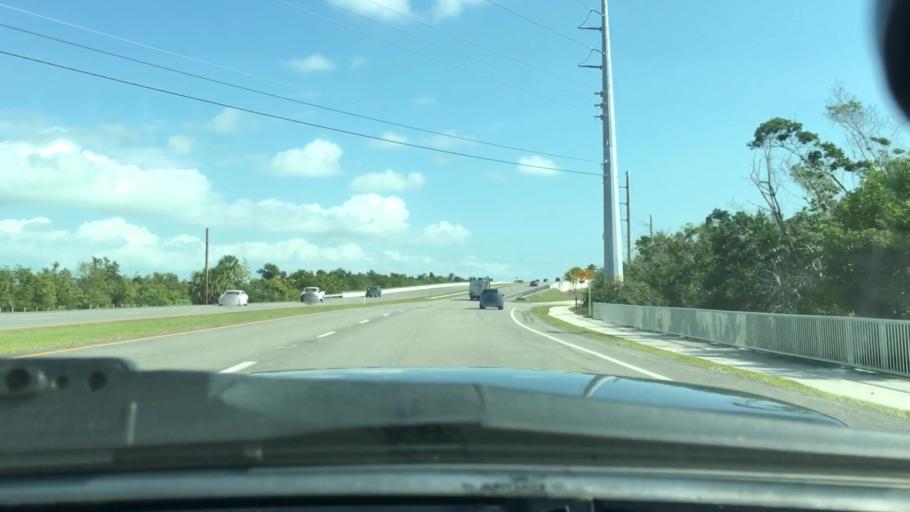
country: US
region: Florida
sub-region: Monroe County
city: Big Coppitt Key
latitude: 24.5873
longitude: -81.6947
